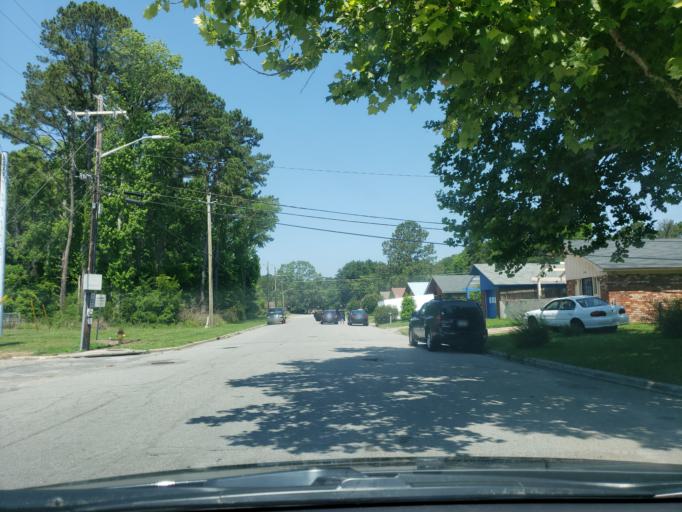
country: US
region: Georgia
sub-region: Chatham County
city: Montgomery
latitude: 31.9947
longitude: -81.1324
